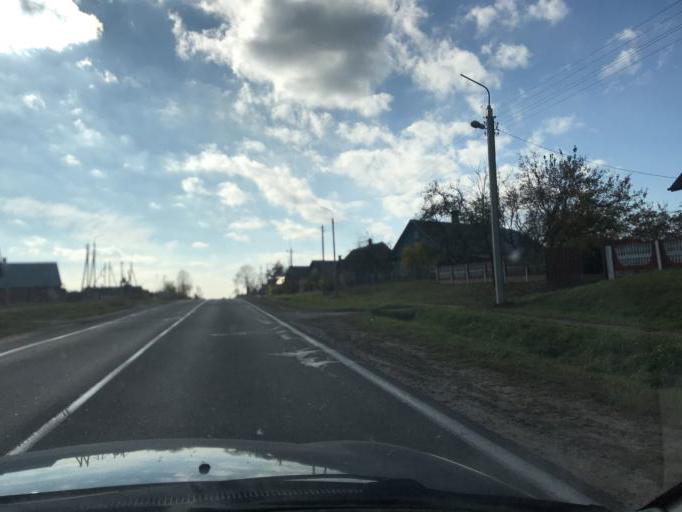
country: LT
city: Salcininkai
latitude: 54.2592
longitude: 25.3572
